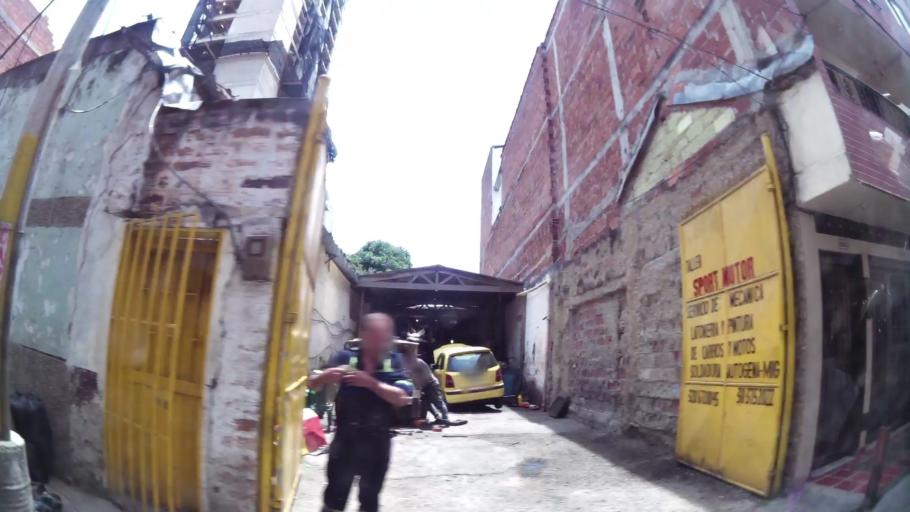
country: CO
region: Antioquia
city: Bello
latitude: 6.3352
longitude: -75.5545
